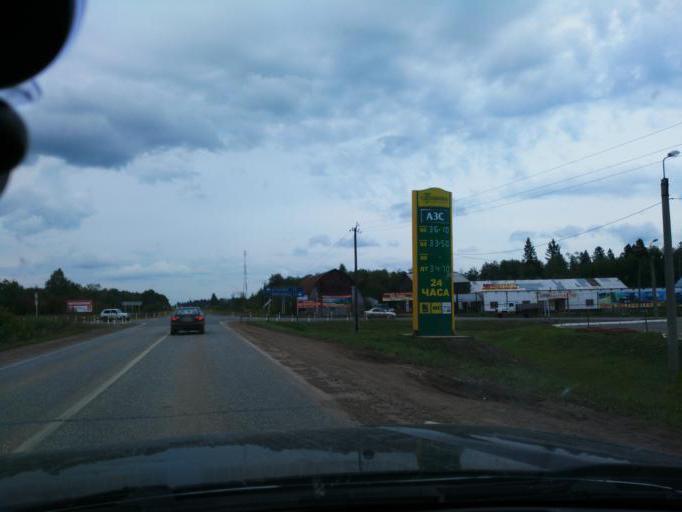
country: RU
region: Perm
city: Chernushka
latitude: 56.5336
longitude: 56.0673
